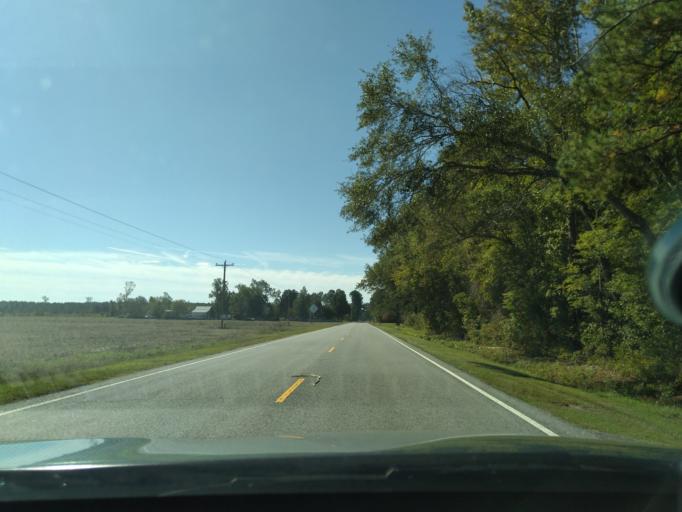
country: US
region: North Carolina
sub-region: Beaufort County
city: Belhaven
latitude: 35.6623
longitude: -76.7917
